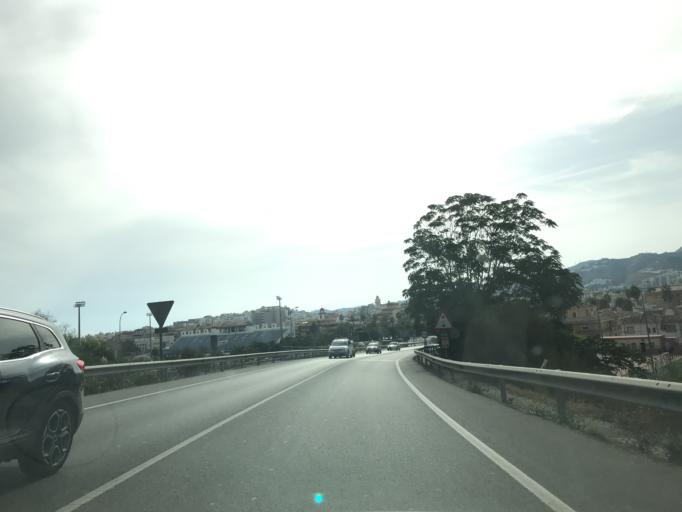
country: ES
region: Andalusia
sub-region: Provincia de Granada
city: Almunecar
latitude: 36.7362
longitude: -3.6805
